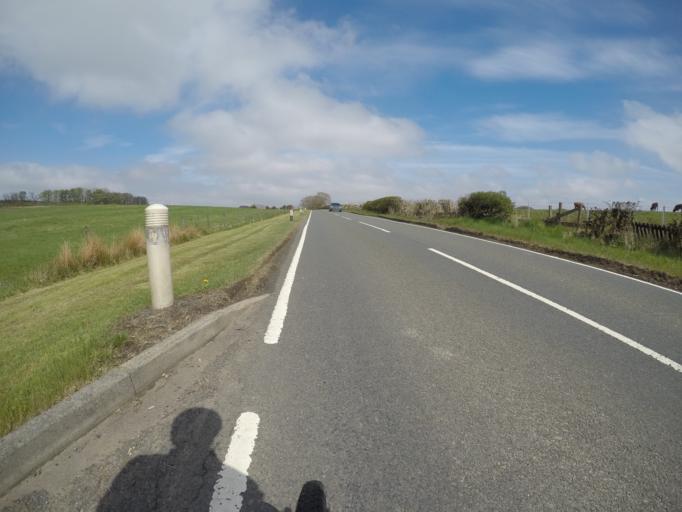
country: GB
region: Scotland
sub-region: East Ayrshire
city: Stewarton
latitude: 55.7081
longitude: -4.4596
